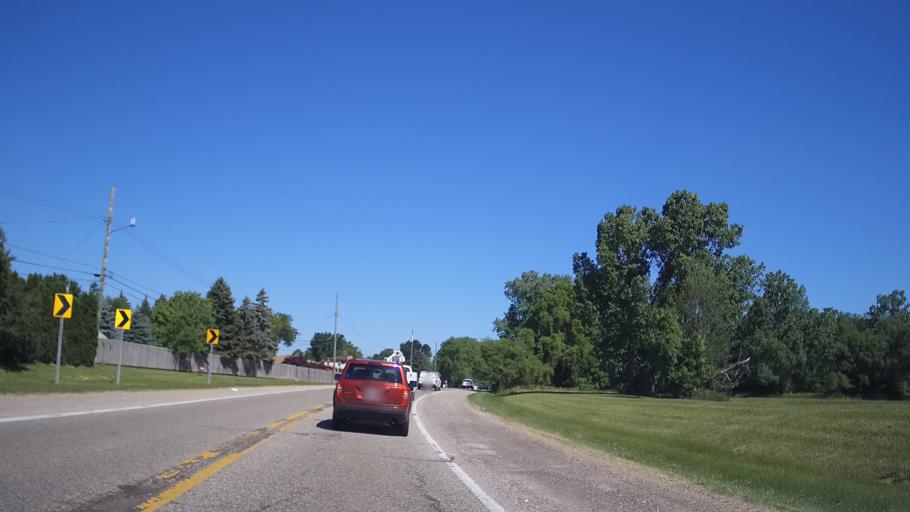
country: US
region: Michigan
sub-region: Macomb County
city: Sterling Heights
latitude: 42.5783
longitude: -82.9921
